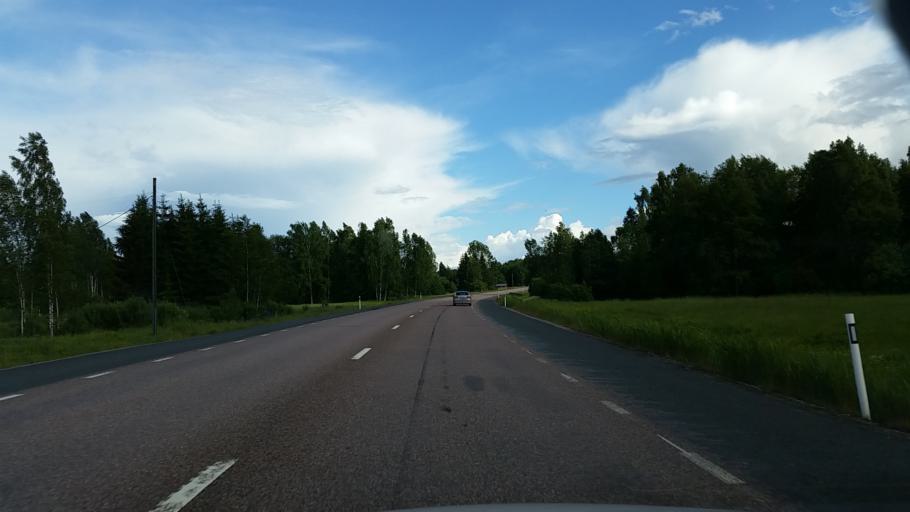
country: SE
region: Dalarna
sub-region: Smedjebackens Kommun
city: Smedjebacken
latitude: 60.0464
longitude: 15.5726
